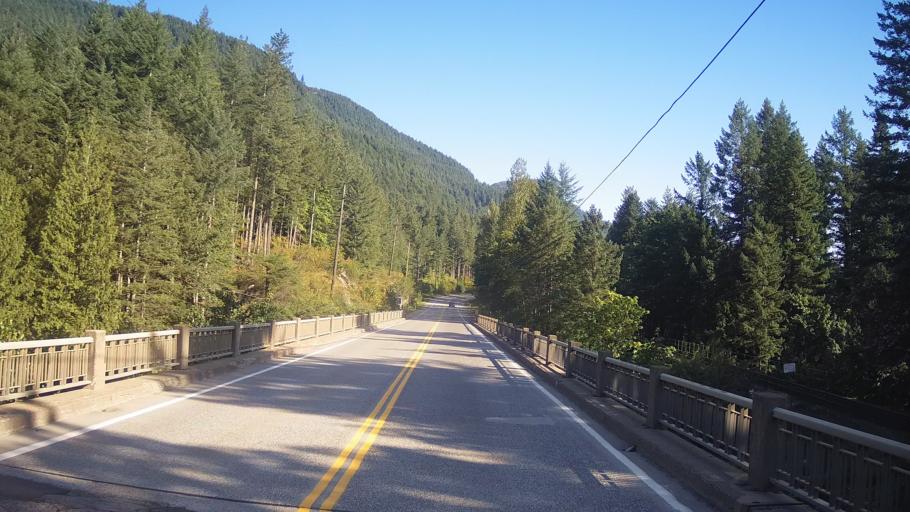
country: CA
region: British Columbia
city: Hope
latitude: 49.4301
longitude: -121.4380
